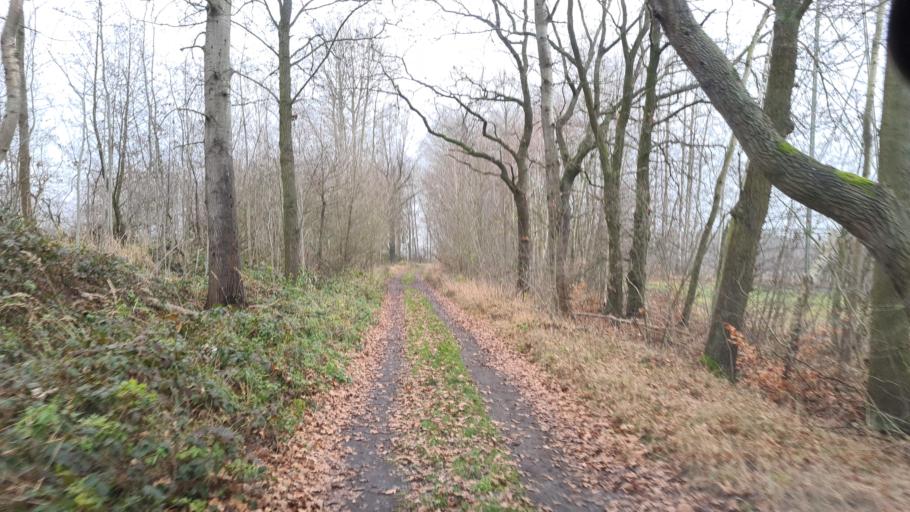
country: DE
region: Brandenburg
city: Doberlug-Kirchhain
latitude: 51.6263
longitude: 13.5329
